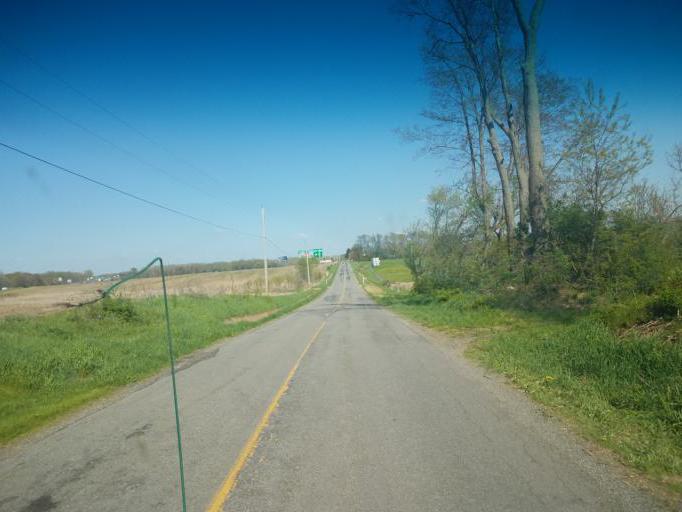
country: US
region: Ohio
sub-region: Medina County
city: Lodi
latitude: 40.9958
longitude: -81.9823
